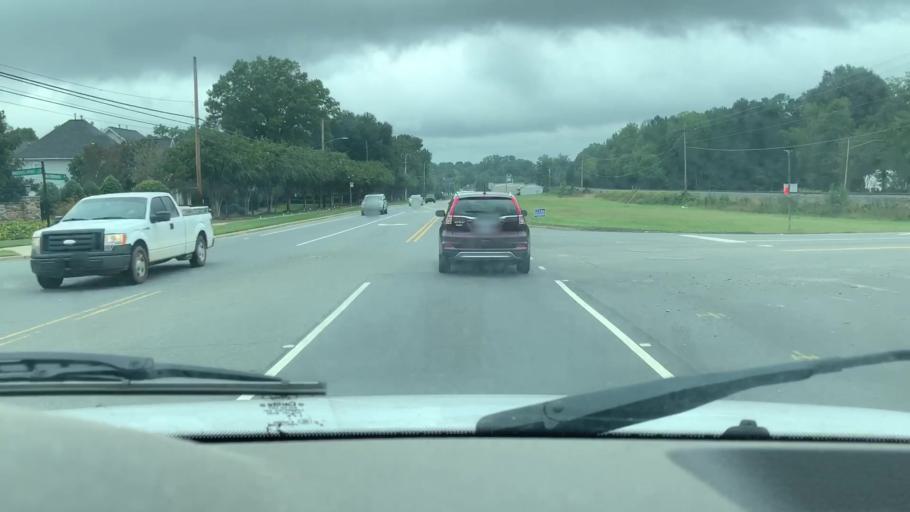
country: US
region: North Carolina
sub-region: Mecklenburg County
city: Huntersville
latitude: 35.3984
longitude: -80.8381
